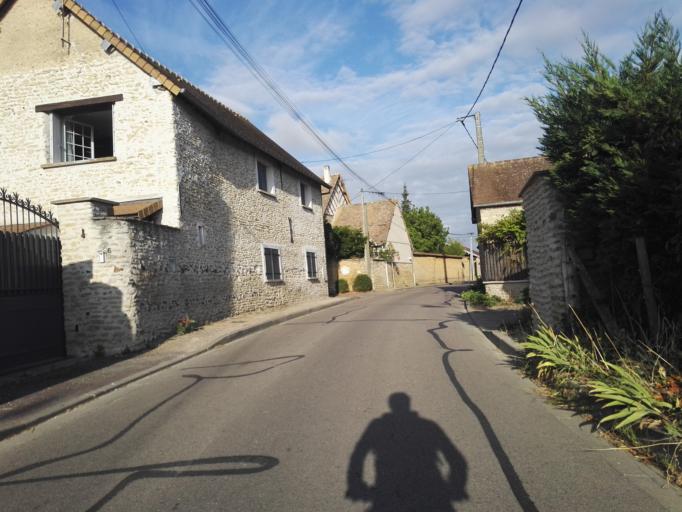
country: FR
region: Haute-Normandie
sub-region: Departement de l'Eure
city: Menilles
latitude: 49.0415
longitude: 1.3219
